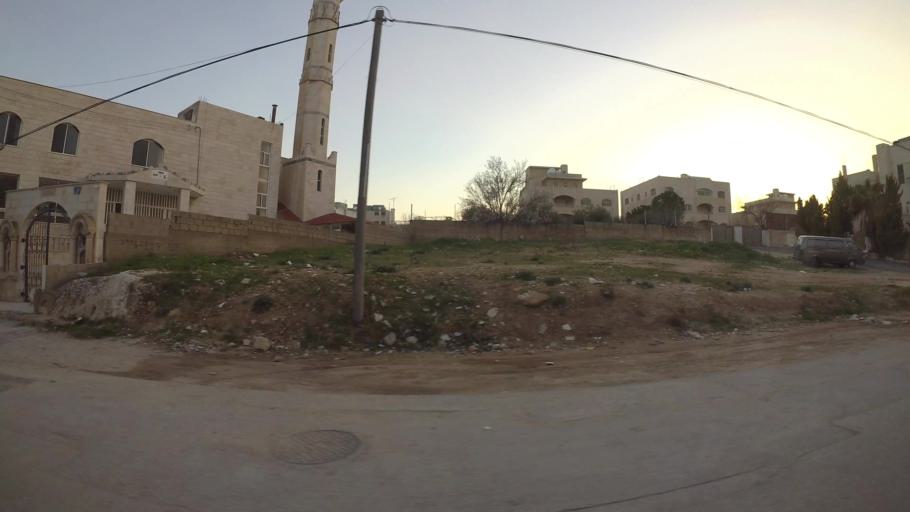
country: JO
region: Amman
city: Al Quwaysimah
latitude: 31.8986
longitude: 35.9297
